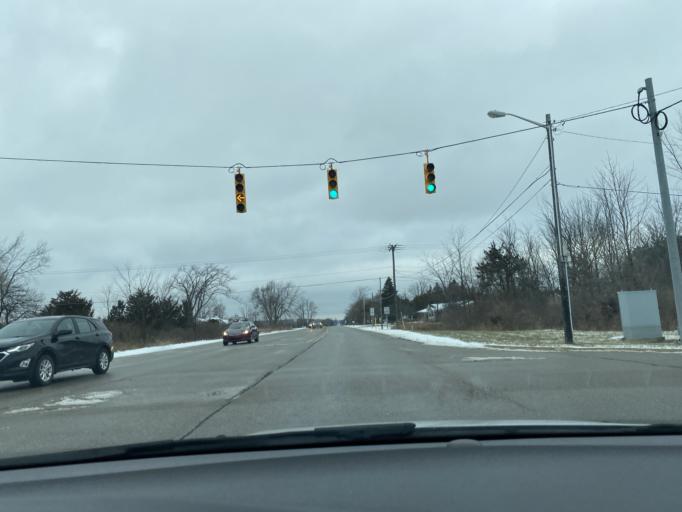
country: US
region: Michigan
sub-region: Lapeer County
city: Lapeer
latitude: 43.0573
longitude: -83.3428
